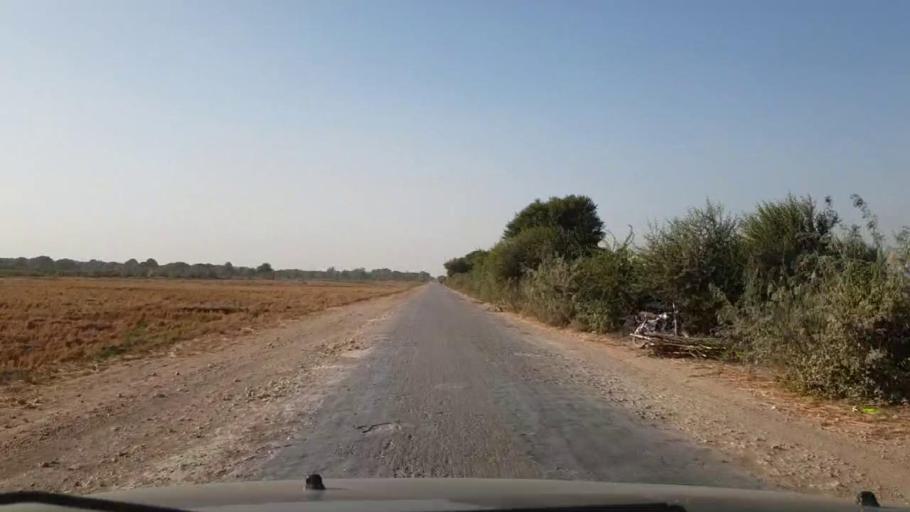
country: PK
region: Sindh
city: Chambar
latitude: 25.2029
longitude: 68.7918
